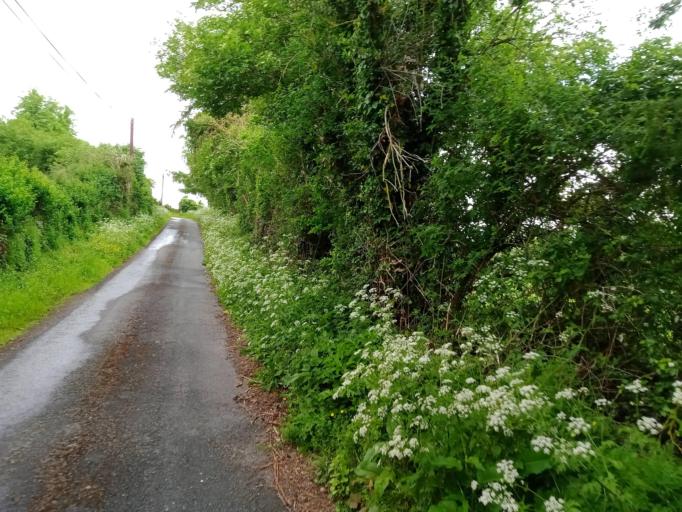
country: IE
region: Leinster
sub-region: Kilkenny
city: Thomastown
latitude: 52.5170
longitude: -7.1357
